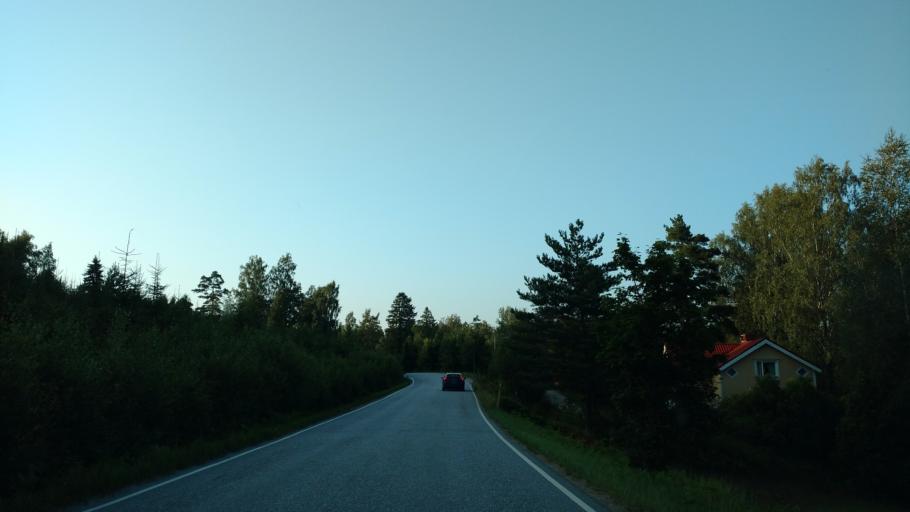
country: FI
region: Varsinais-Suomi
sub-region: Aboland-Turunmaa
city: Dragsfjaerd
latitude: 60.0631
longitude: 22.4516
